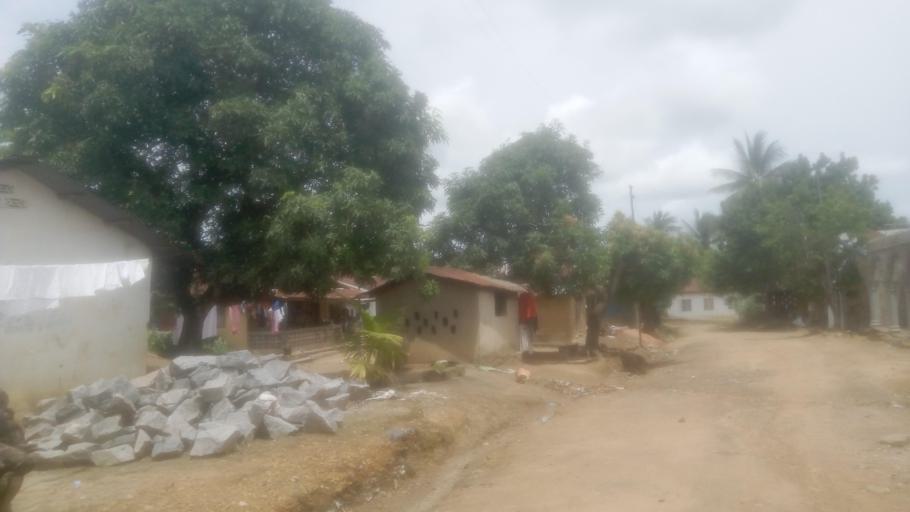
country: SL
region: Southern Province
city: Bo
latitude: 7.9544
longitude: -11.7145
